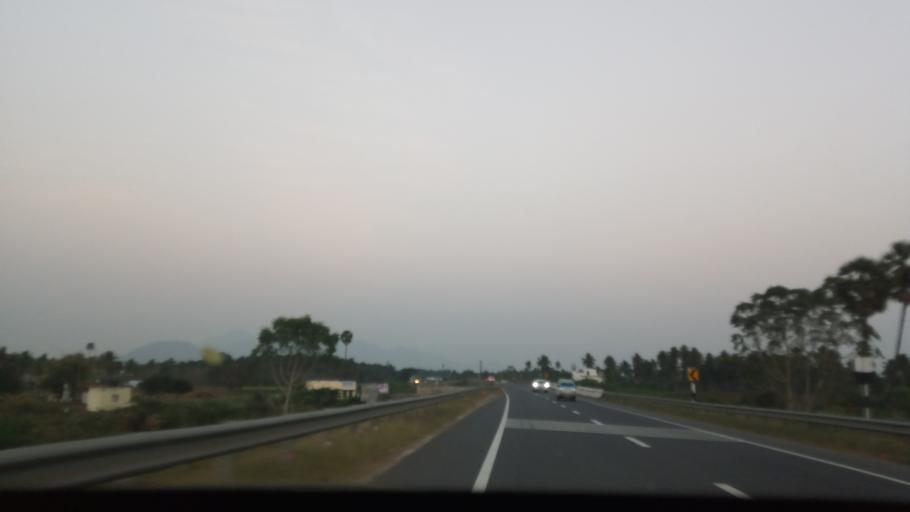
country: IN
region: Tamil Nadu
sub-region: Salem
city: Belur
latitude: 11.6497
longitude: 78.4034
